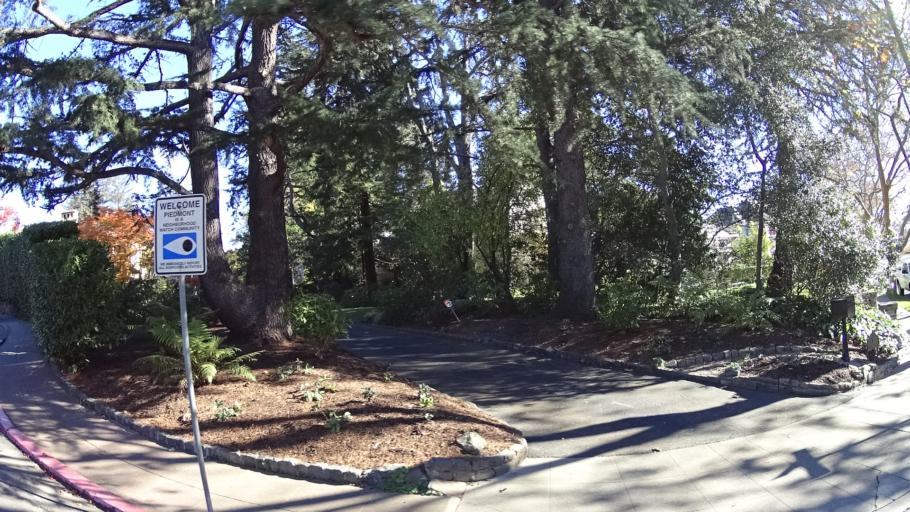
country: US
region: California
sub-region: Alameda County
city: Piedmont
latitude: 37.8227
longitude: -122.2237
